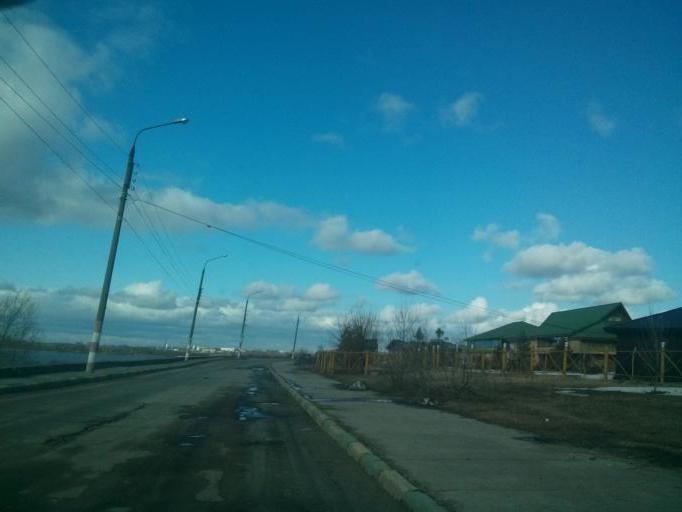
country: RU
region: Nizjnij Novgorod
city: Nizhniy Novgorod
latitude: 56.3311
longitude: 44.0327
